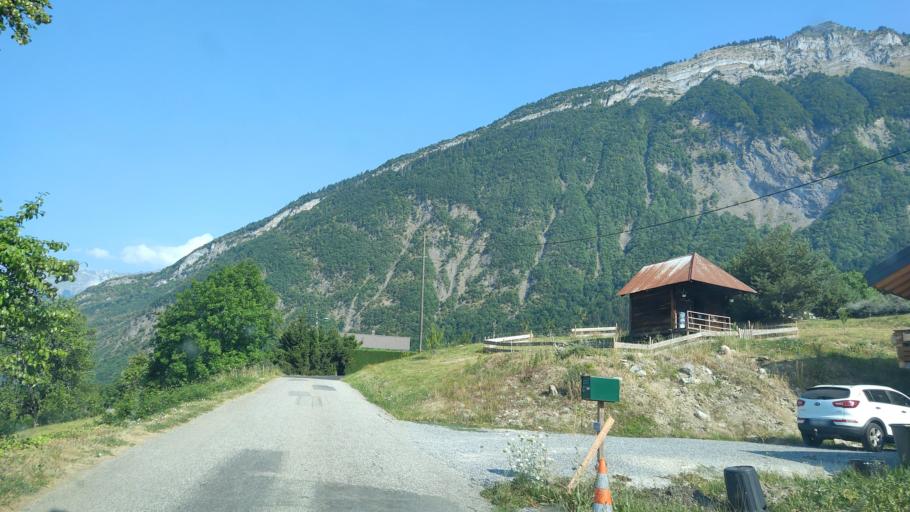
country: FR
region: Rhone-Alpes
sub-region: Departement de la Savoie
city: Ugine
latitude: 45.7651
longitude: 6.4012
